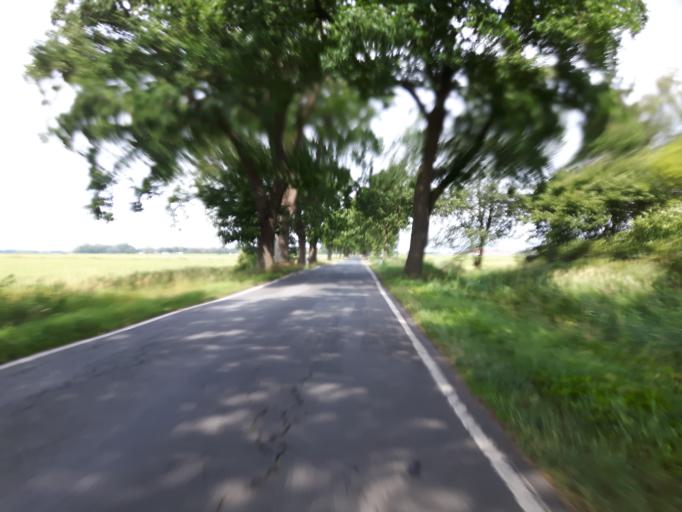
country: DE
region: Lower Saxony
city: Rastede
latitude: 53.3322
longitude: 8.2569
